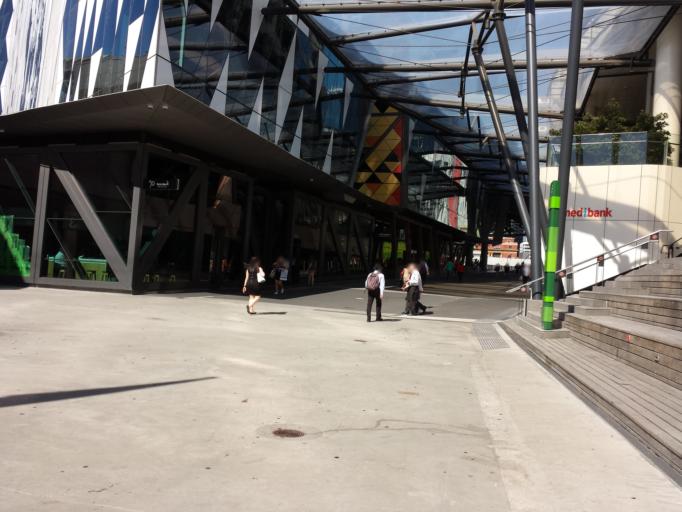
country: AU
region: Victoria
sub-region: Melbourne
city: Docklands
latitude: -37.8180
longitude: 144.9486
